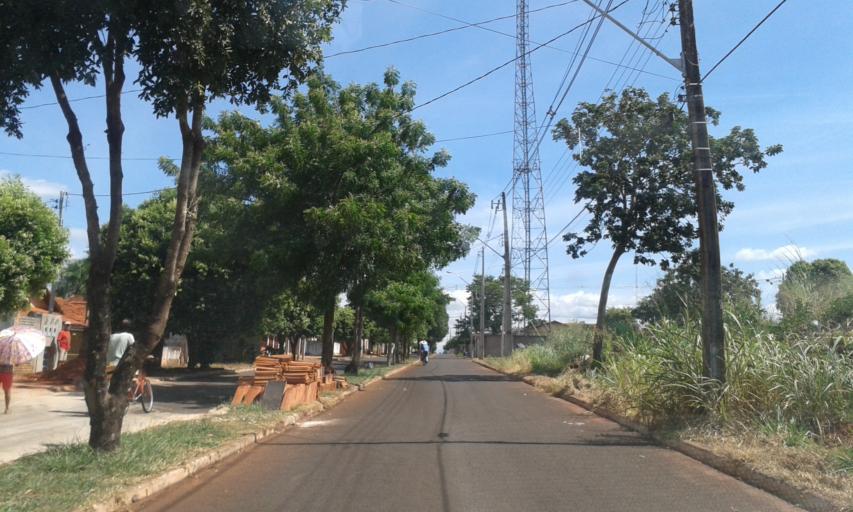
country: BR
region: Minas Gerais
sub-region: Santa Vitoria
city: Santa Vitoria
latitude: -18.8480
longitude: -50.1199
